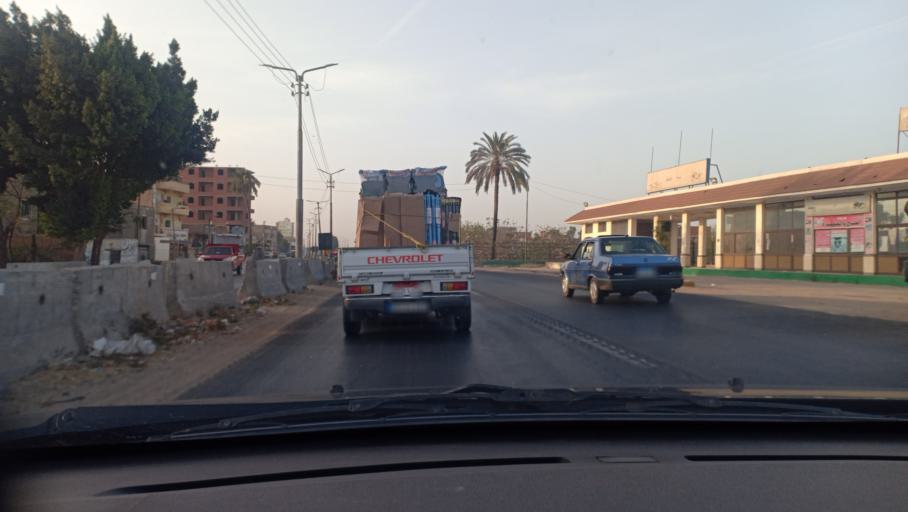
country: EG
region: Muhafazat al Minufiyah
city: Quwaysina
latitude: 30.5415
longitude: 31.2693
